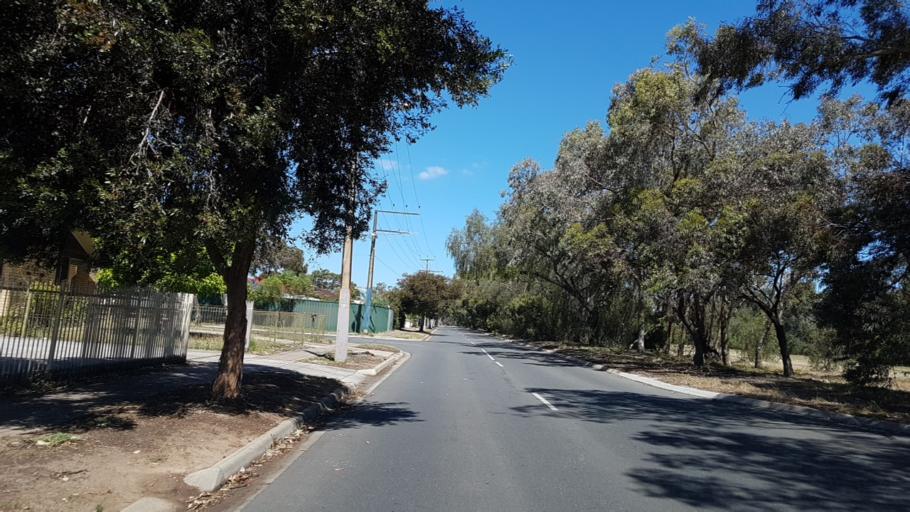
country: AU
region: South Australia
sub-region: Salisbury
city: Salisbury
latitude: -34.7938
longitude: 138.6070
